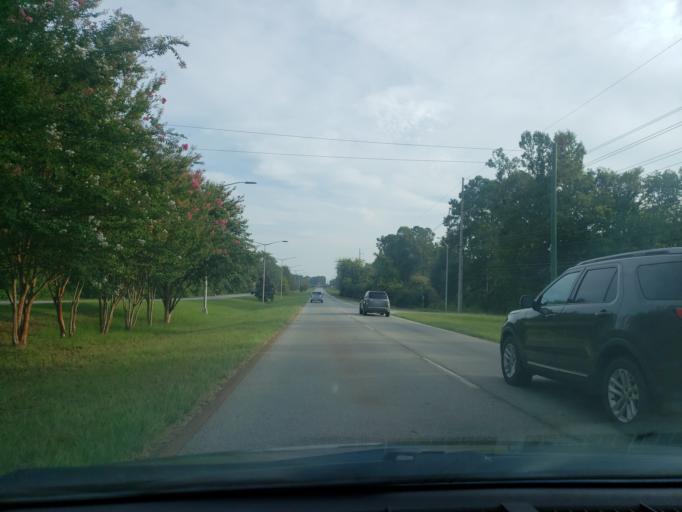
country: US
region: Georgia
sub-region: Dougherty County
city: Albany
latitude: 31.5929
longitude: -84.2194
